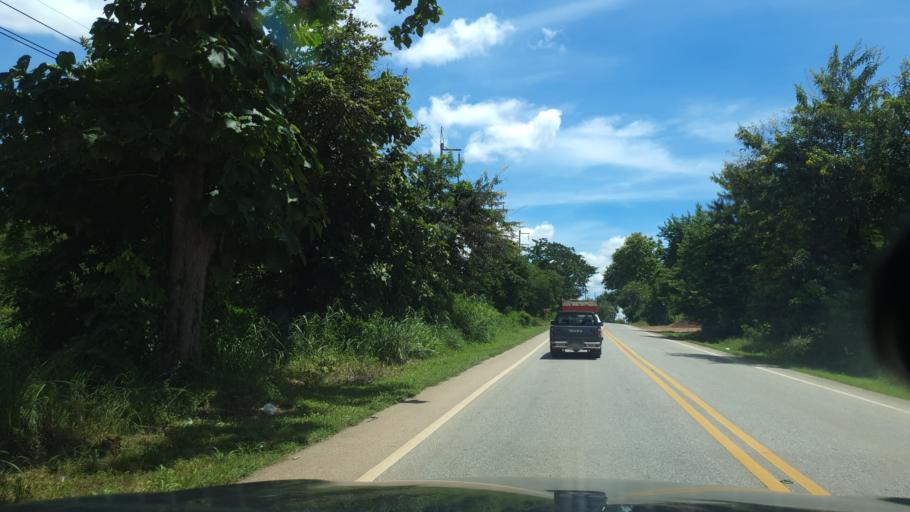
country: TH
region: Sukhothai
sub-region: Amphoe Si Satchanalai
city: Si Satchanalai
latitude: 17.4402
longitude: 99.7974
